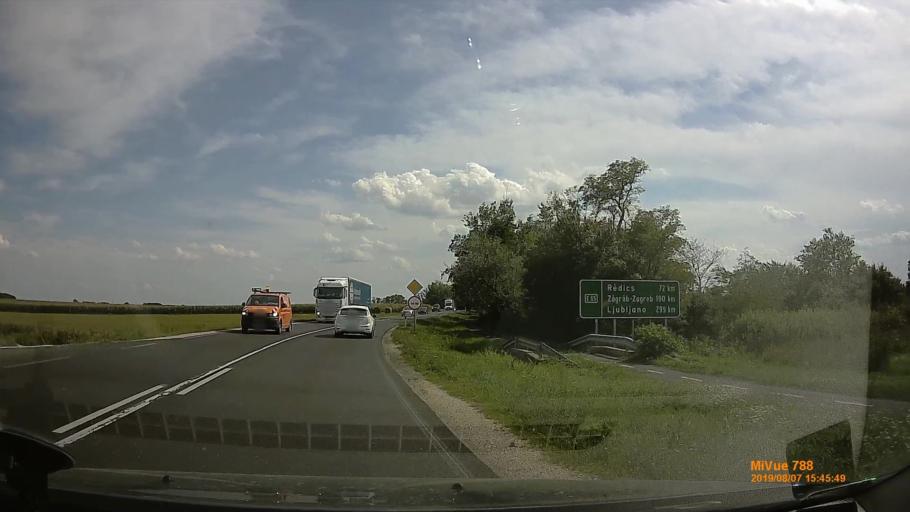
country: HU
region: Vas
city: Szombathely
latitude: 47.1925
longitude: 16.6203
